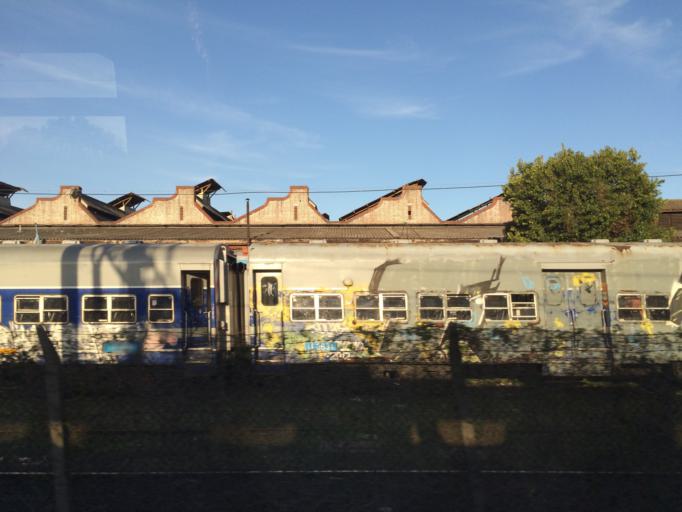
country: AR
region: Buenos Aires
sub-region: Partido de Lanus
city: Lanus
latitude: -34.7247
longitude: -58.3932
